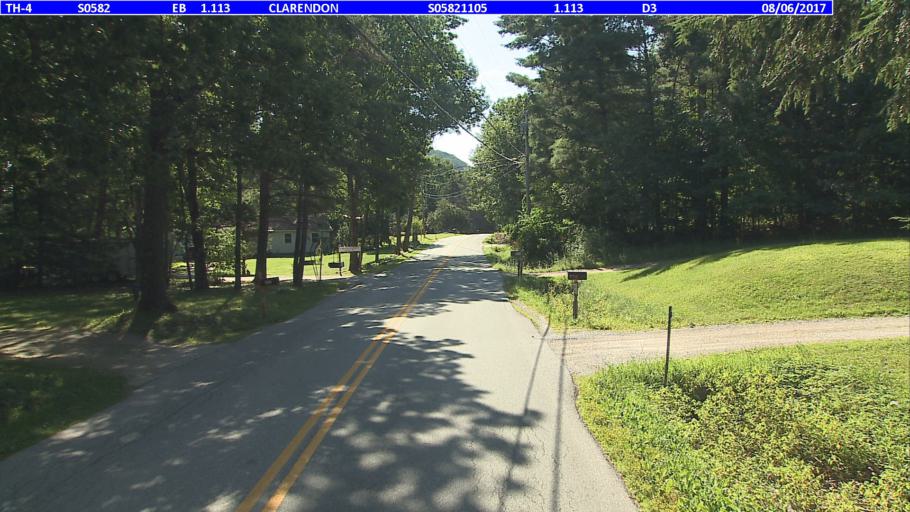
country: US
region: Vermont
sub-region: Rutland County
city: Rutland
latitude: 43.5653
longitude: -72.9440
